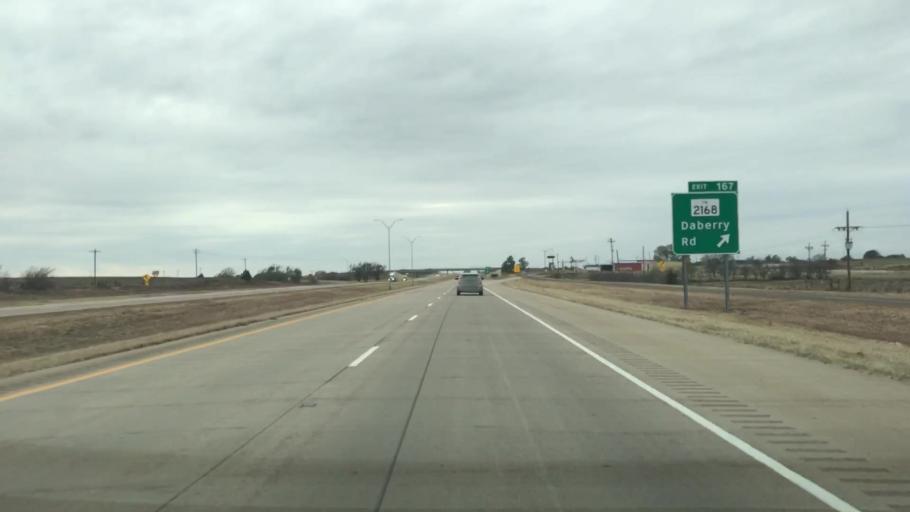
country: US
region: Texas
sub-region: Wheeler County
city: Shamrock
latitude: 35.2270
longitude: -100.1573
